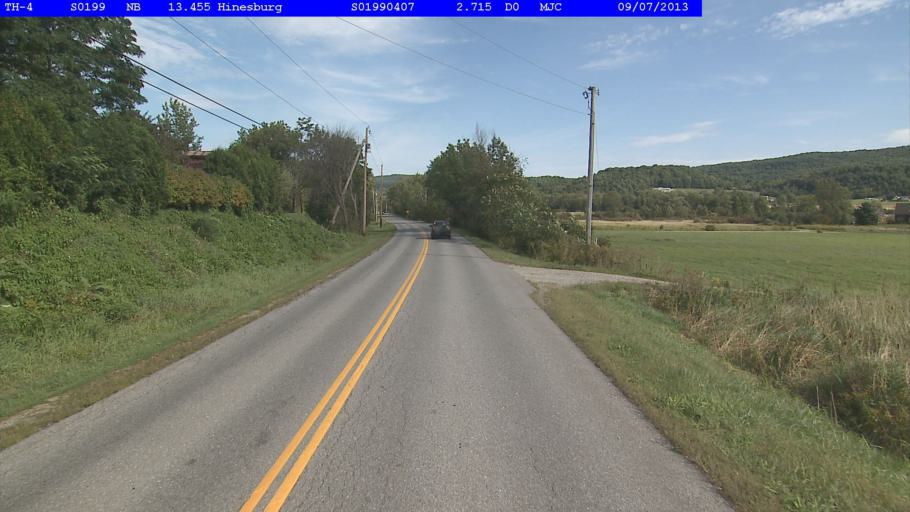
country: US
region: Vermont
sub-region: Chittenden County
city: Hinesburg
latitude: 44.3169
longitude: -73.1100
